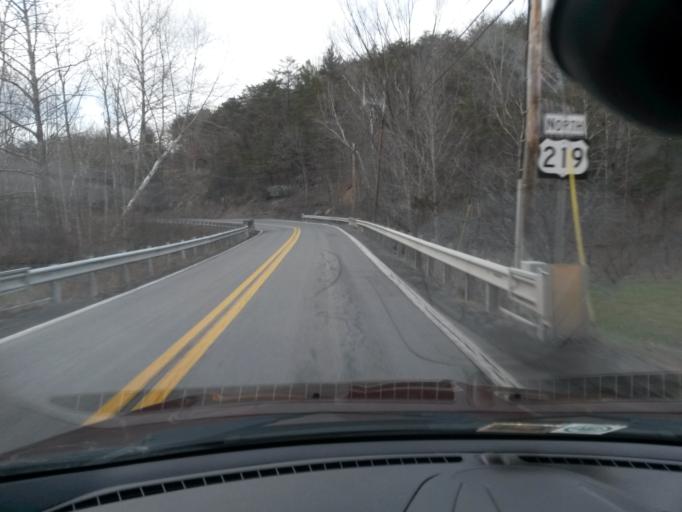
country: US
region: West Virginia
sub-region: Monroe County
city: Union
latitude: 37.4985
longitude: -80.6072
